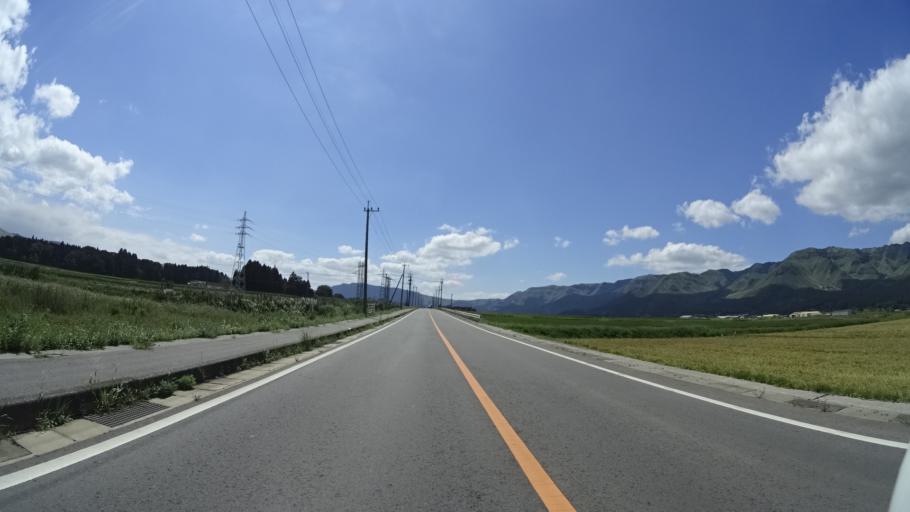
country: JP
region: Kumamoto
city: Aso
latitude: 32.9452
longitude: 131.0288
